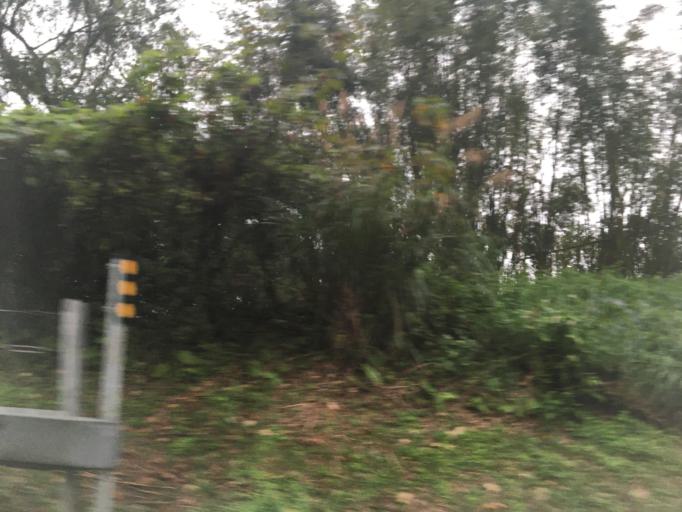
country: TW
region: Taiwan
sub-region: Keelung
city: Keelung
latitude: 25.0354
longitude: 121.8611
